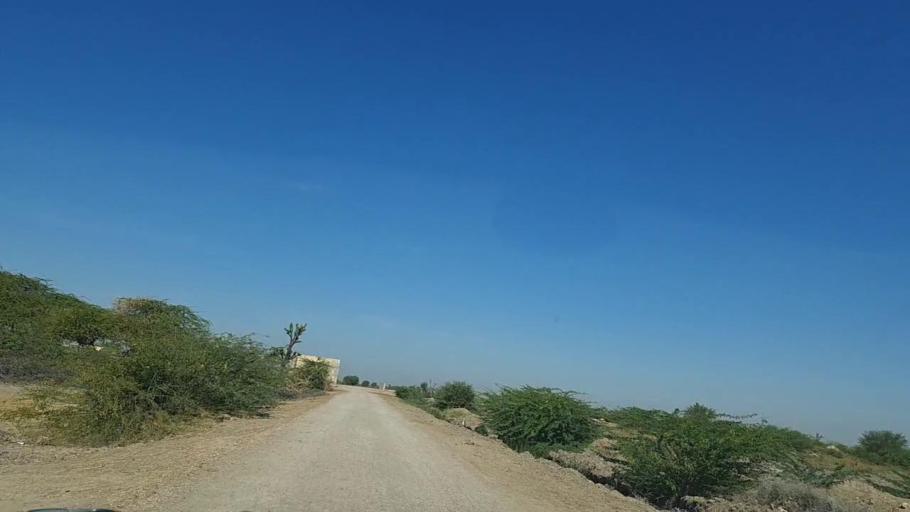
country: PK
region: Sindh
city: Dhoro Naro
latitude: 25.4870
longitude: 69.5269
